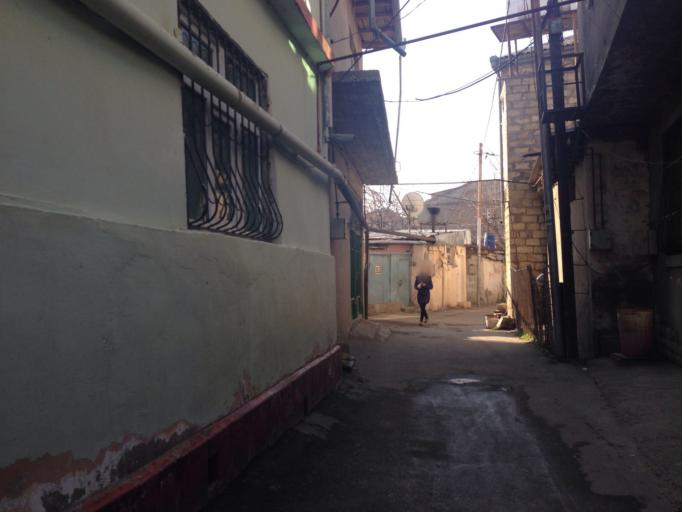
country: AZ
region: Baki
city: Baku
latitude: 40.3978
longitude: 49.8829
